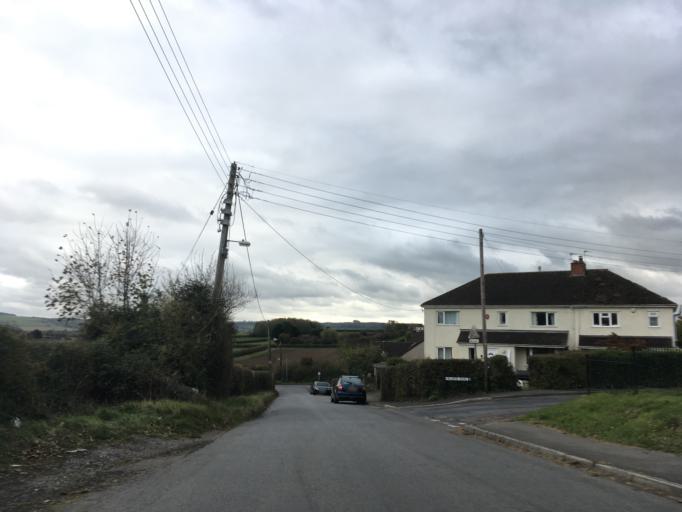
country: GB
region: England
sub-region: South Gloucestershire
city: Pucklechurch
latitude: 51.4871
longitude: -2.4306
